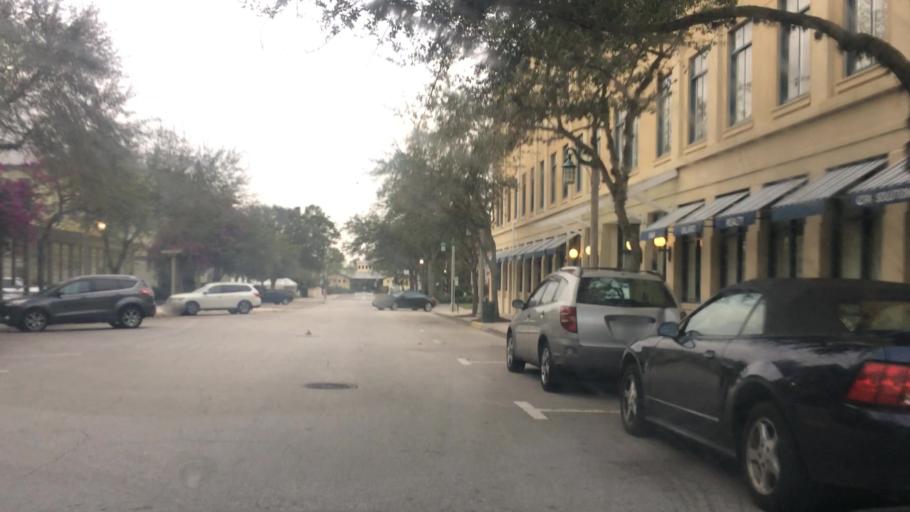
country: US
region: Florida
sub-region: Osceola County
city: Celebration
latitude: 28.3189
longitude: -81.5393
